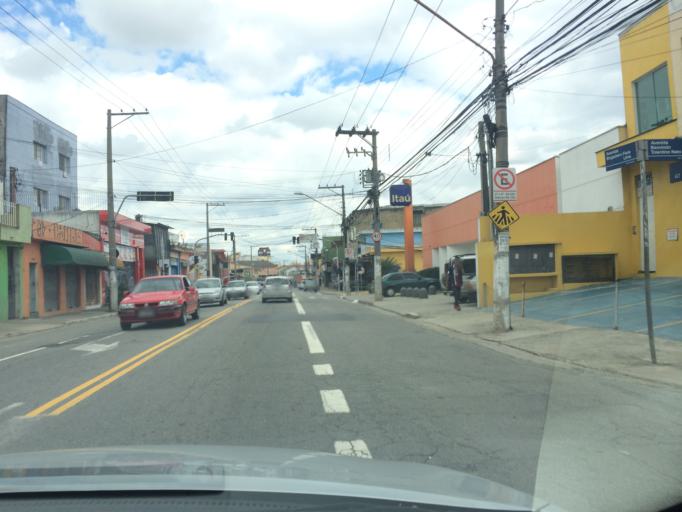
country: BR
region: Sao Paulo
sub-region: Guarulhos
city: Guarulhos
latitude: -23.4513
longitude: -46.5205
